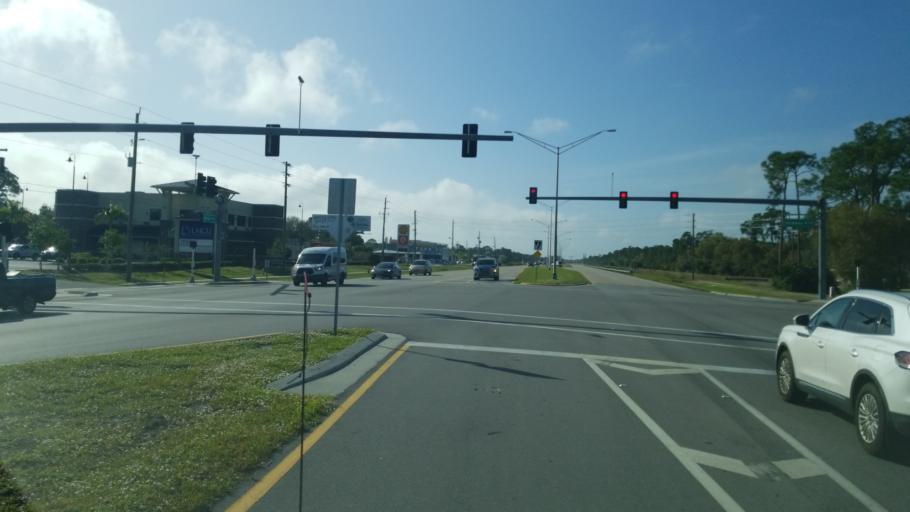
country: US
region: Florida
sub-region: Charlotte County
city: Port Charlotte
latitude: 26.9996
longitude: -82.0569
